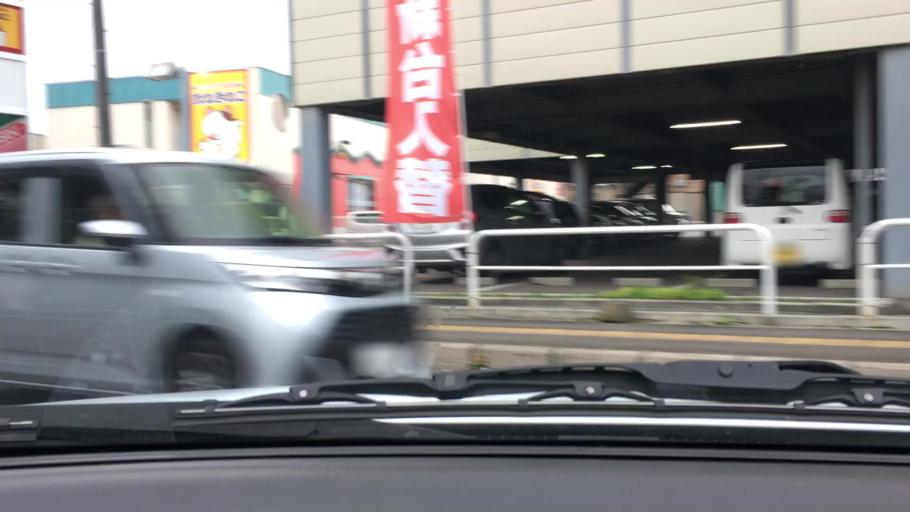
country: JP
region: Hokkaido
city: Hakodate
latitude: 41.8021
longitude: 140.7309
